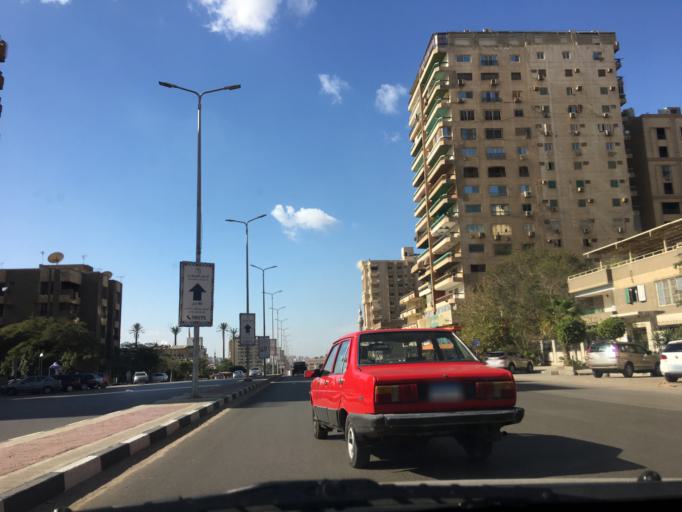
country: EG
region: Muhafazat al Qahirah
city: Cairo
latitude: 30.0529
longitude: 31.3303
